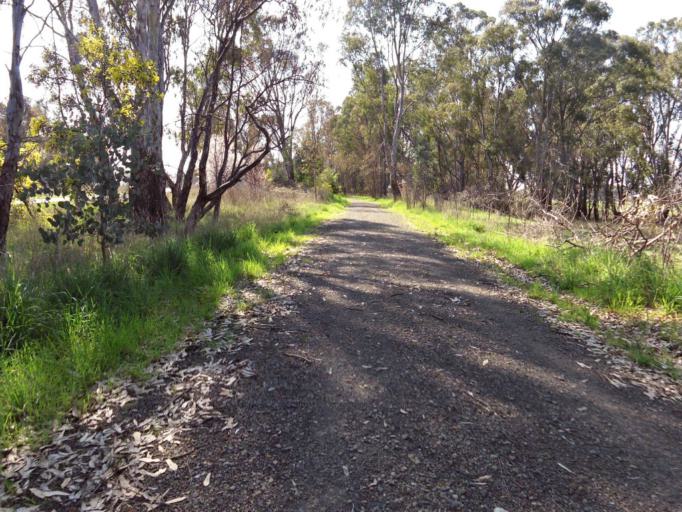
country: AU
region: Victoria
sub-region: Murrindindi
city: Alexandra
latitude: -37.1514
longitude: 145.5807
